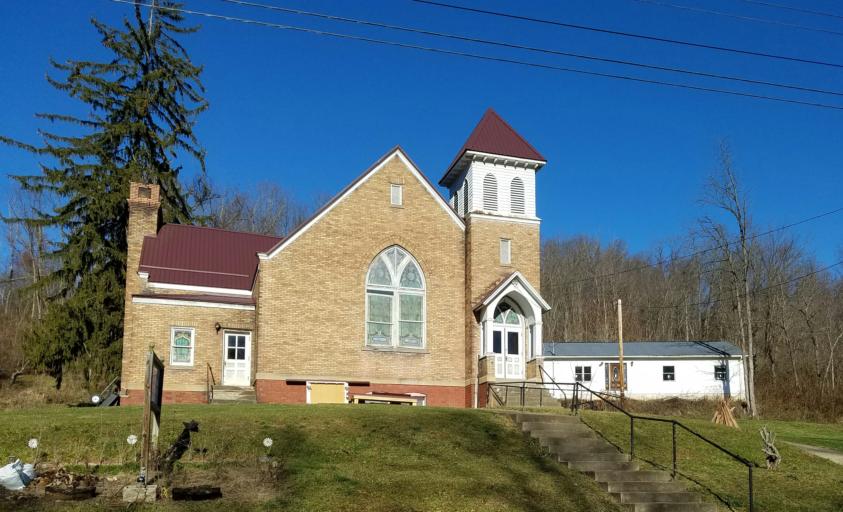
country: US
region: Ohio
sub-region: Belmont County
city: Barnesville
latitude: 40.0615
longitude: -81.1643
